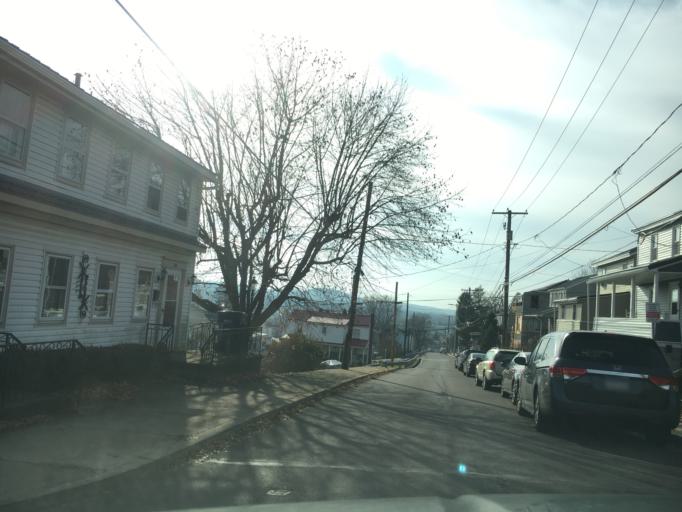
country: US
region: Pennsylvania
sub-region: Montour County
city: Danville
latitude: 40.9676
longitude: -76.6102
